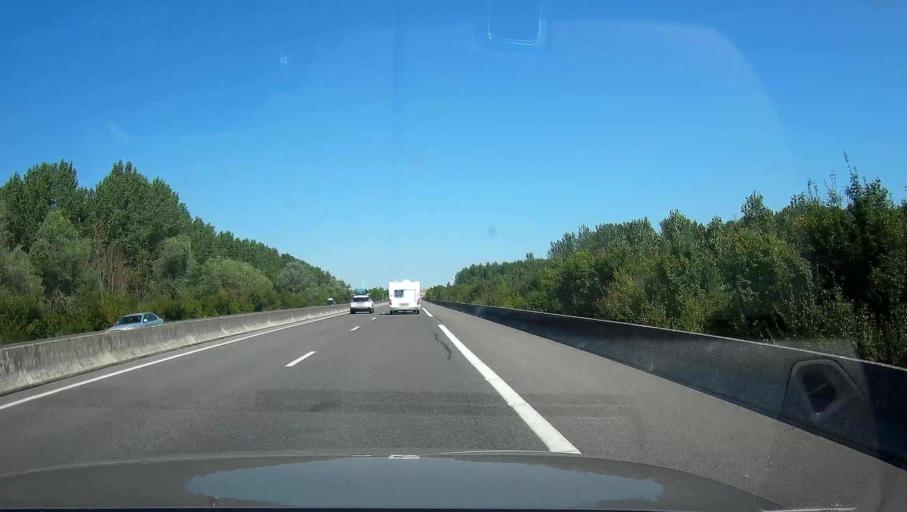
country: FR
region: Champagne-Ardenne
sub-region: Departement de l'Aube
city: Arcis-sur-Aube
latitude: 48.5398
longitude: 4.1865
